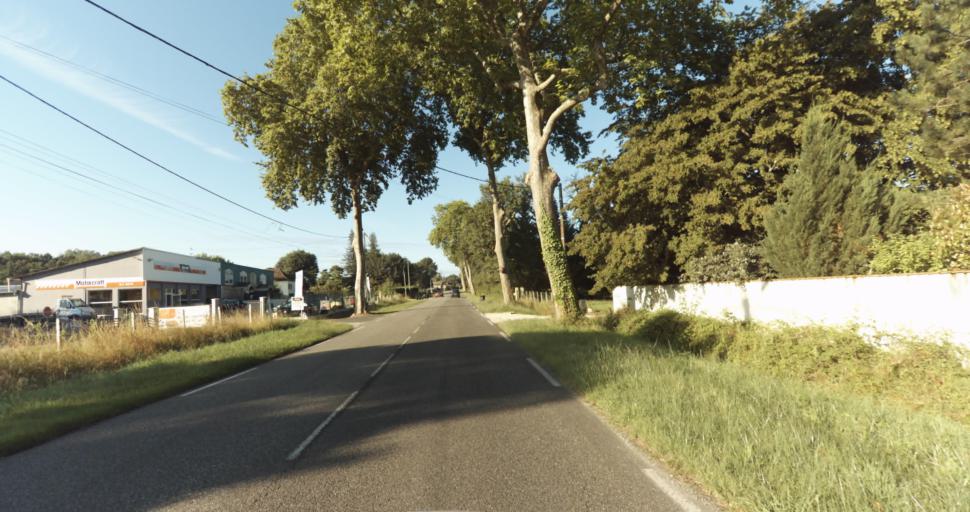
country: FR
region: Aquitaine
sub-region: Departement de la Gironde
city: Bazas
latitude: 44.4215
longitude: -0.2151
